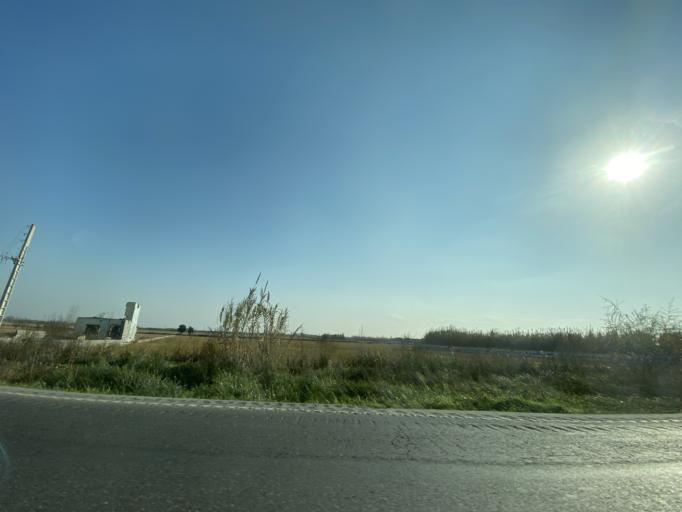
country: IR
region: Mazandaran
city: Babol
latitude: 36.5004
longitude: 52.5234
